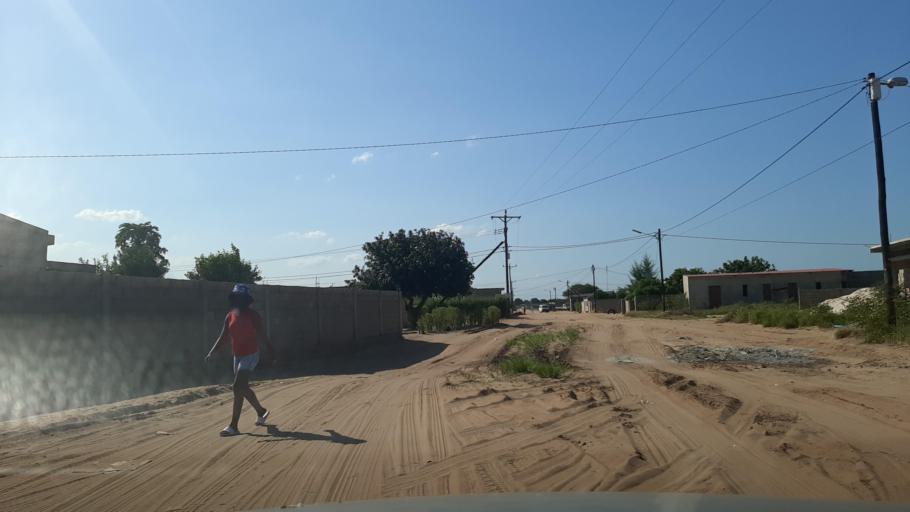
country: MZ
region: Maputo
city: Matola
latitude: -25.7997
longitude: 32.4909
